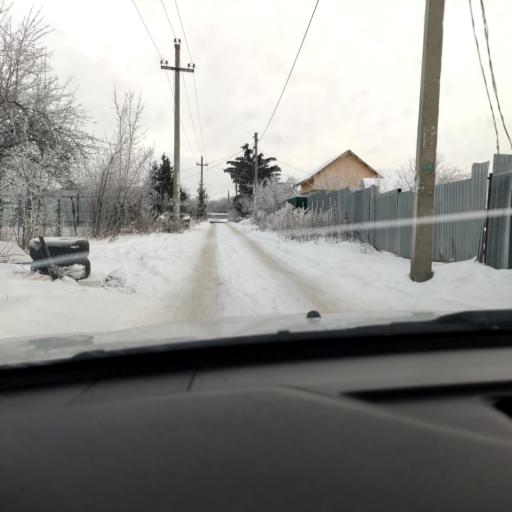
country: RU
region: Samara
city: Petra-Dubrava
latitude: 53.3014
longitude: 50.2499
